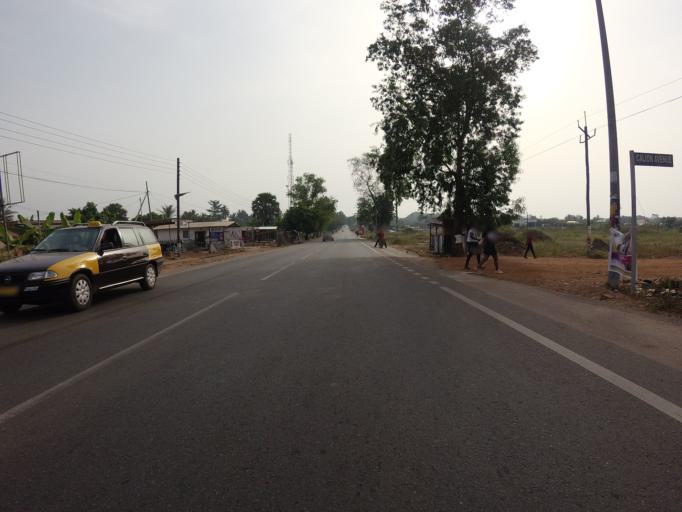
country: GH
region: Volta
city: Ho
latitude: 6.6031
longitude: 0.4862
